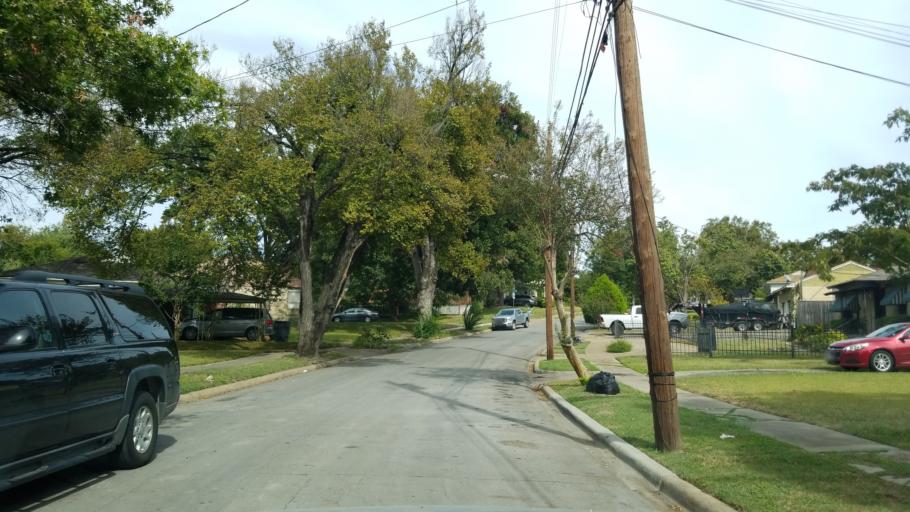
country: US
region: Texas
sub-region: Dallas County
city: Dallas
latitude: 32.7698
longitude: -96.7249
